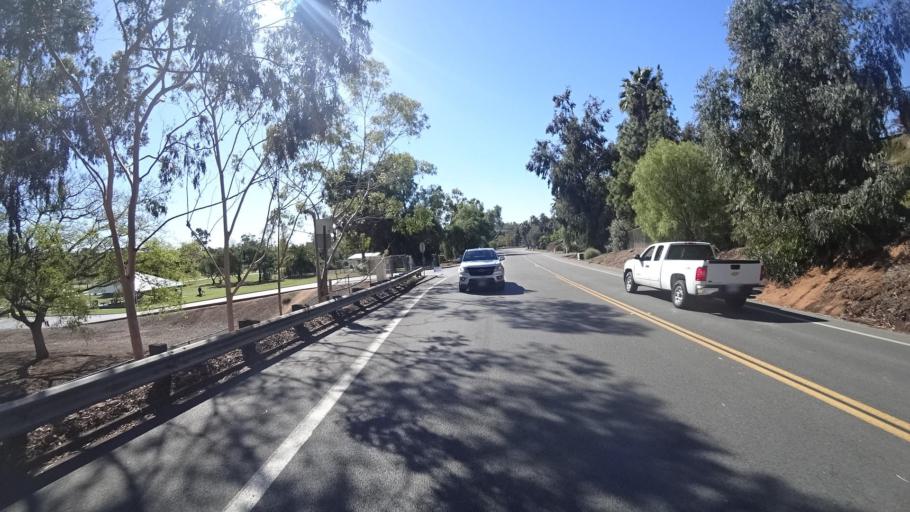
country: US
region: California
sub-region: San Diego County
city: Bonita
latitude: 32.6657
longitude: -117.0341
